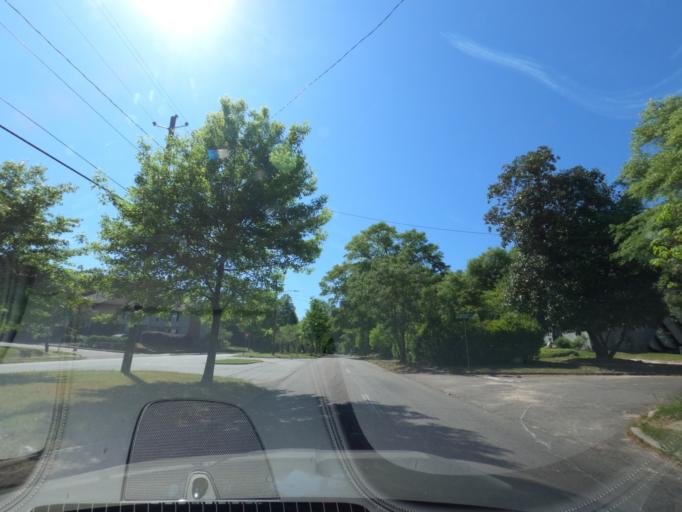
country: US
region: Georgia
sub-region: Richmond County
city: Augusta
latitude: 33.4706
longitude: -82.0189
